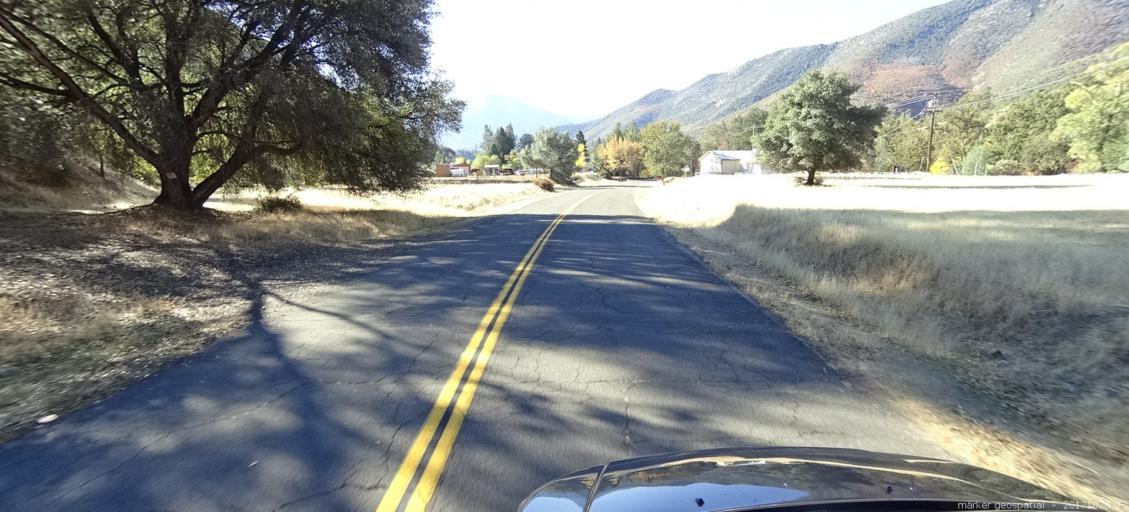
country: US
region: California
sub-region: Trinity County
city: Lewiston
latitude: 40.7068
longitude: -122.6348
